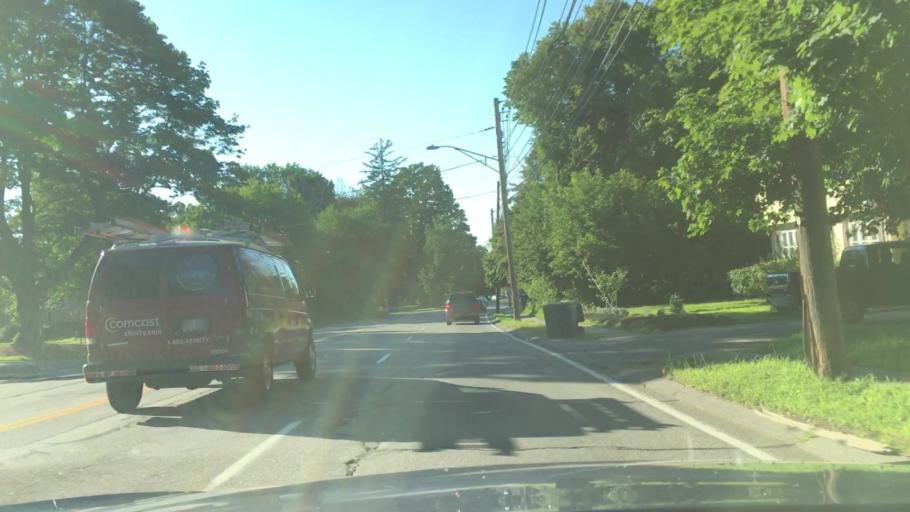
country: US
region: Massachusetts
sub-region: Middlesex County
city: Billerica
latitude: 42.5641
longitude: -71.2714
